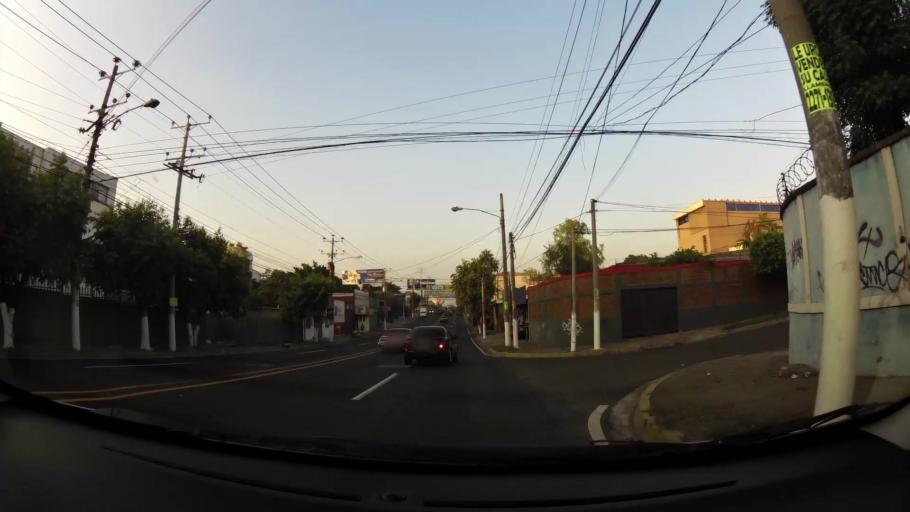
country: SV
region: San Salvador
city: San Salvador
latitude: 13.6943
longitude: -89.2167
